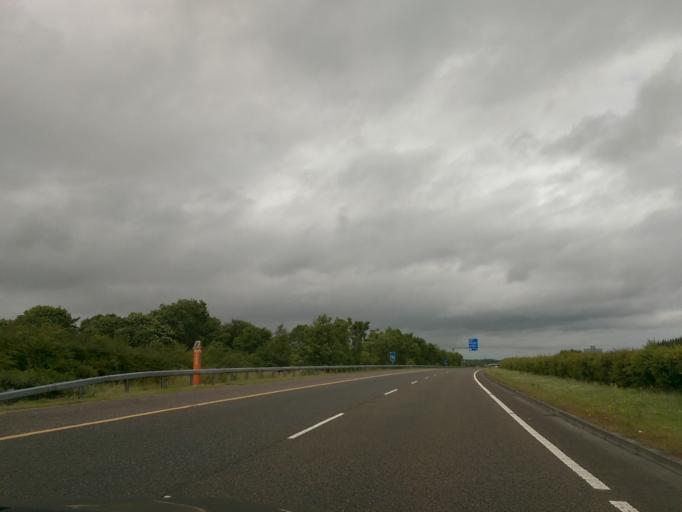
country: IE
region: Munster
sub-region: An Clar
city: Newmarket on Fergus
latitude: 52.7814
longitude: -8.9218
